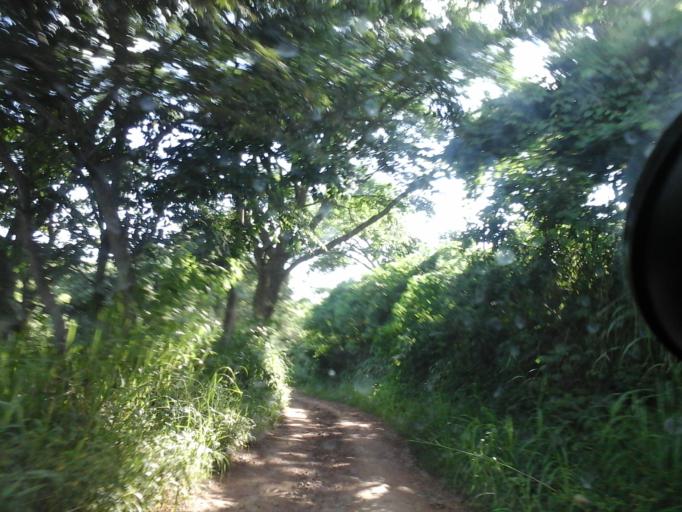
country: CO
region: Cesar
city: San Diego
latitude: 10.2710
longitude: -73.0948
